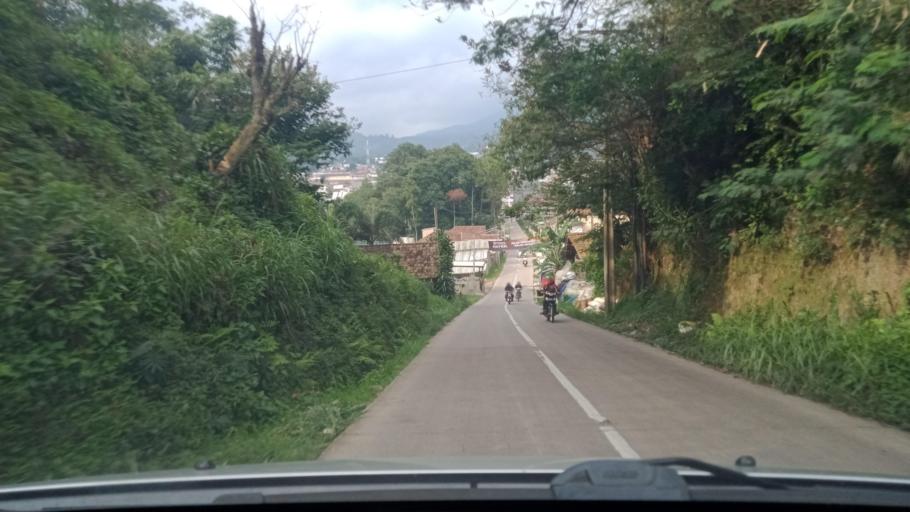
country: ID
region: West Java
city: Lembang
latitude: -6.8170
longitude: 107.5753
